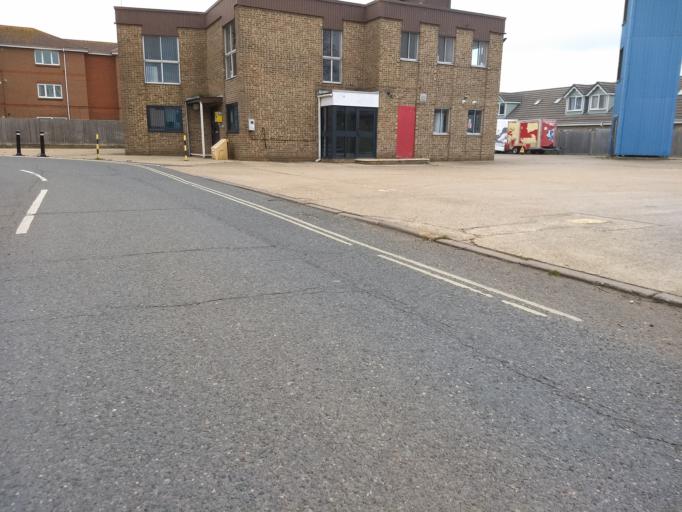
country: GB
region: England
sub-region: Isle of Wight
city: Sandown
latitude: 50.6631
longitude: -1.1502
